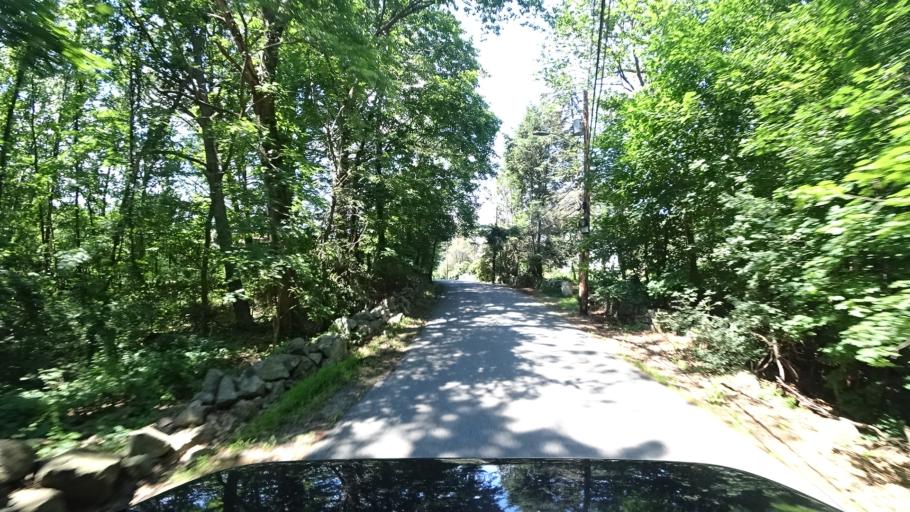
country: US
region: Massachusetts
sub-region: Norfolk County
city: Dedham
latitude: 42.2466
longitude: -71.1861
